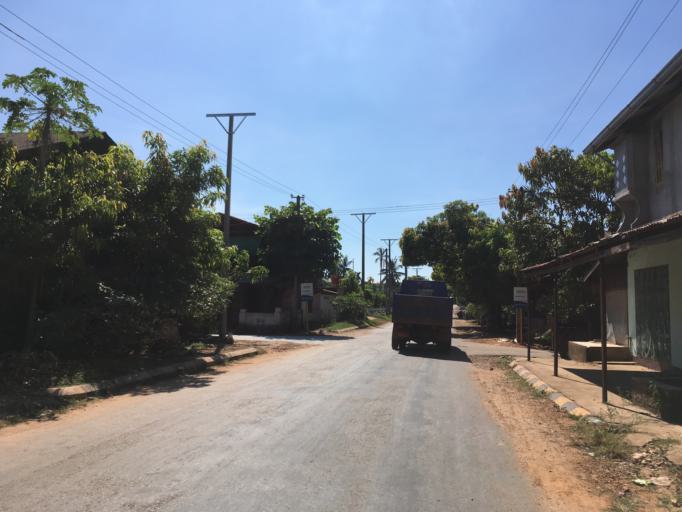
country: MM
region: Mon
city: Kyaikkami
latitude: 15.5051
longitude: 97.8378
